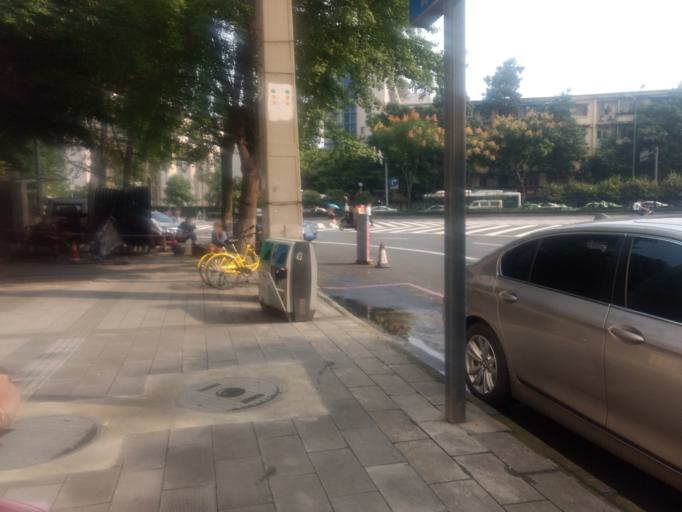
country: CN
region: Sichuan
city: Chengdu
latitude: 30.6731
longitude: 104.0682
